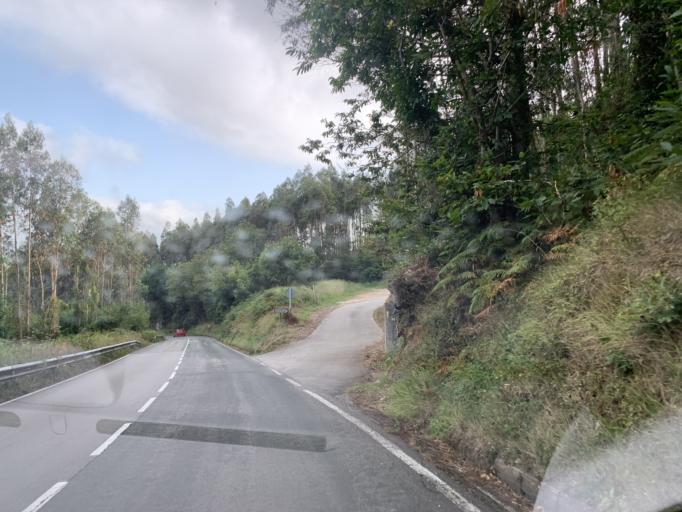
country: ES
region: Asturias
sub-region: Province of Asturias
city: Villaviciosa
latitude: 43.5075
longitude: -5.4272
